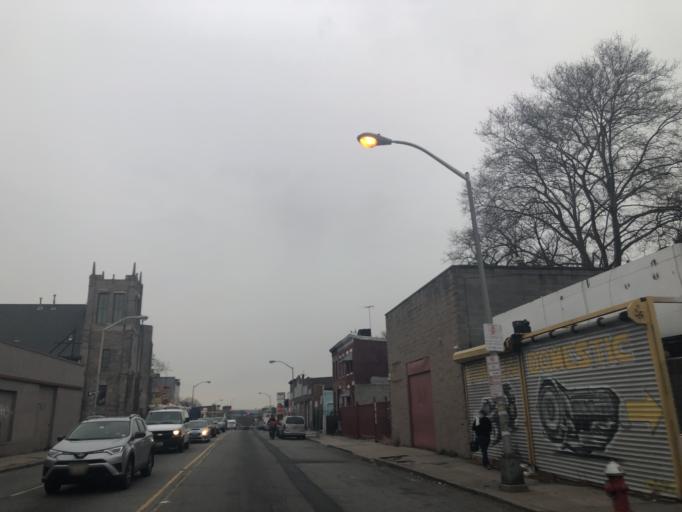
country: US
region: New Jersey
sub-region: Hudson County
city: Jersey City
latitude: 40.7186
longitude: -74.0756
